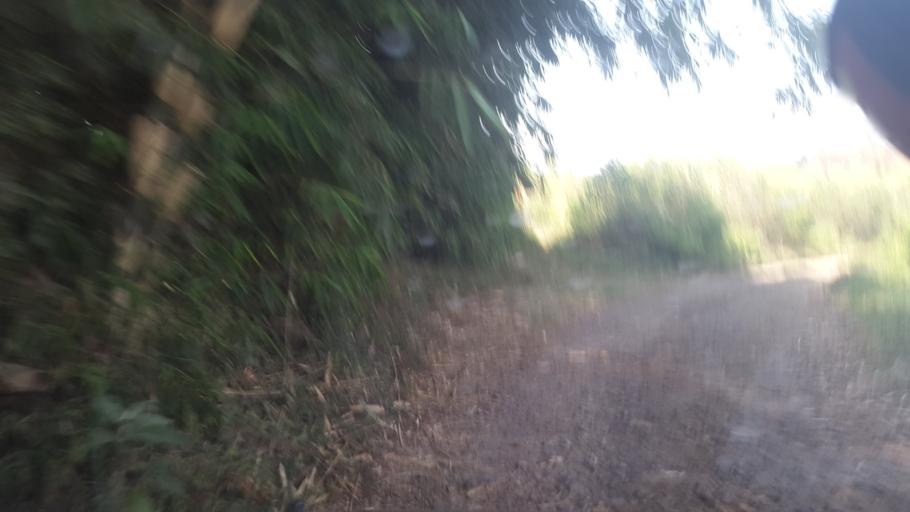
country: ID
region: West Java
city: Pasirreungit
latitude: -7.0128
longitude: 107.0146
